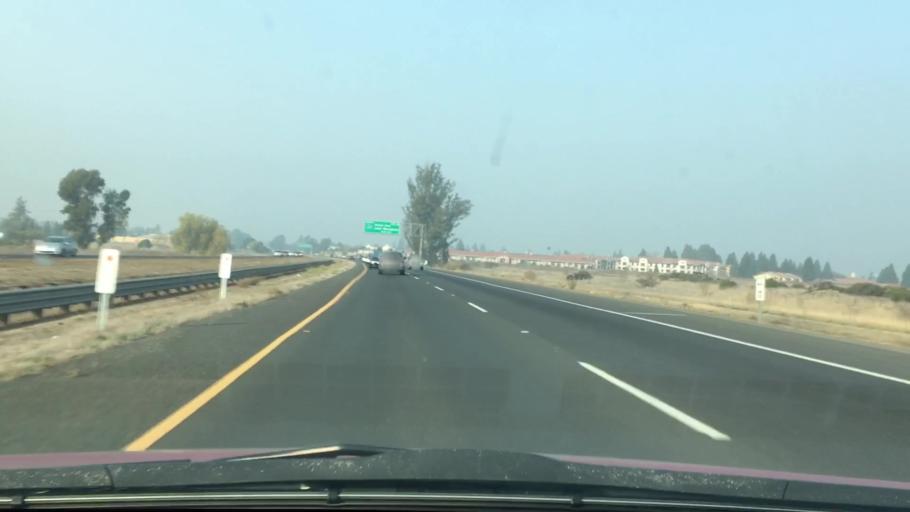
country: US
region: California
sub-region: Napa County
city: Napa
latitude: 38.2700
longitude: -122.2985
